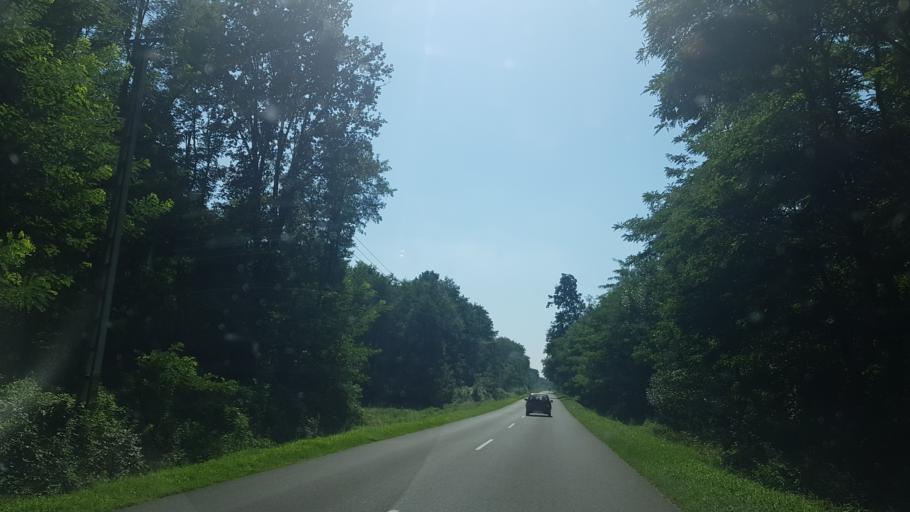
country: HU
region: Somogy
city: Segesd
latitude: 46.3128
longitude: 17.3136
